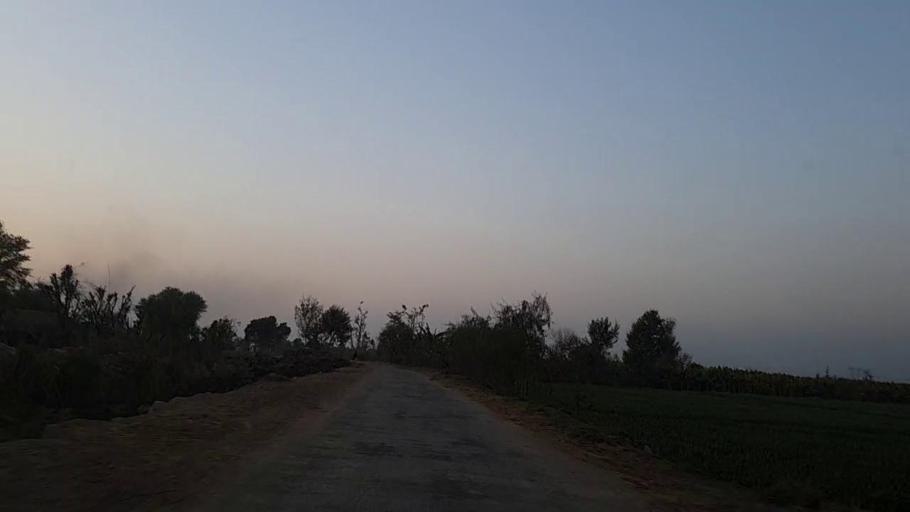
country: PK
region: Sindh
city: Hala
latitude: 25.9561
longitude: 68.4230
